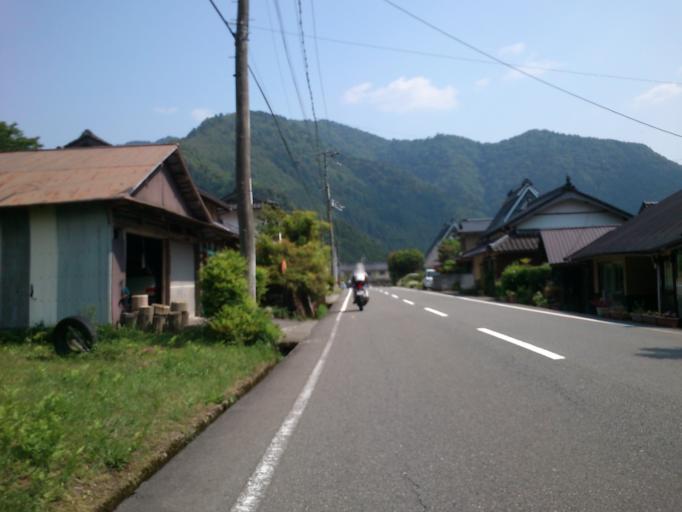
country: JP
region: Kyoto
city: Kameoka
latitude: 35.2674
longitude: 135.5715
